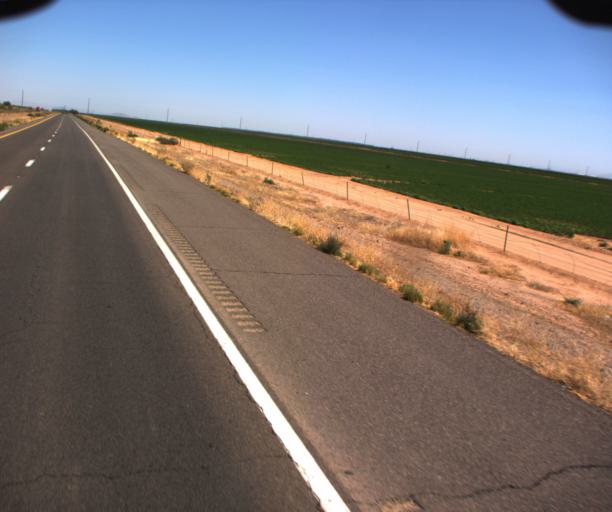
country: US
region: Arizona
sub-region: Pinal County
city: Maricopa
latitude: 32.9459
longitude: -112.0481
